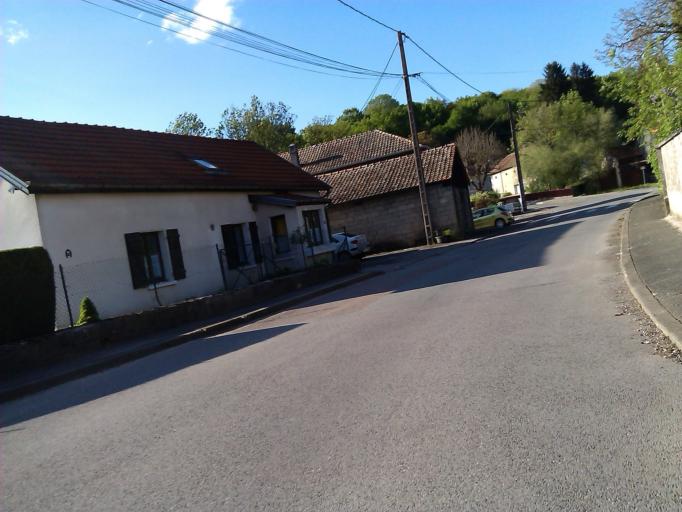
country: FR
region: Franche-Comte
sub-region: Departement du Doubs
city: Clerval
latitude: 47.4424
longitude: 6.5631
